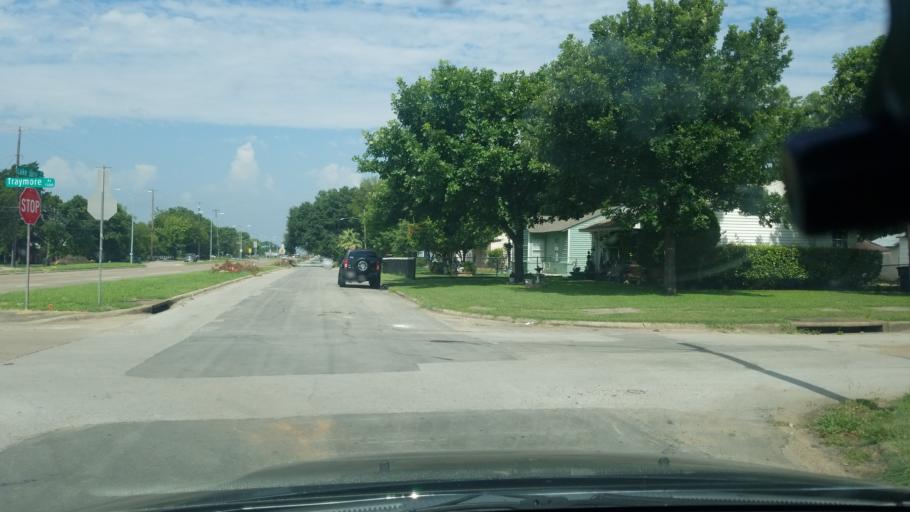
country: US
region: Texas
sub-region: Dallas County
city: Balch Springs
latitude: 32.7345
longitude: -96.6930
